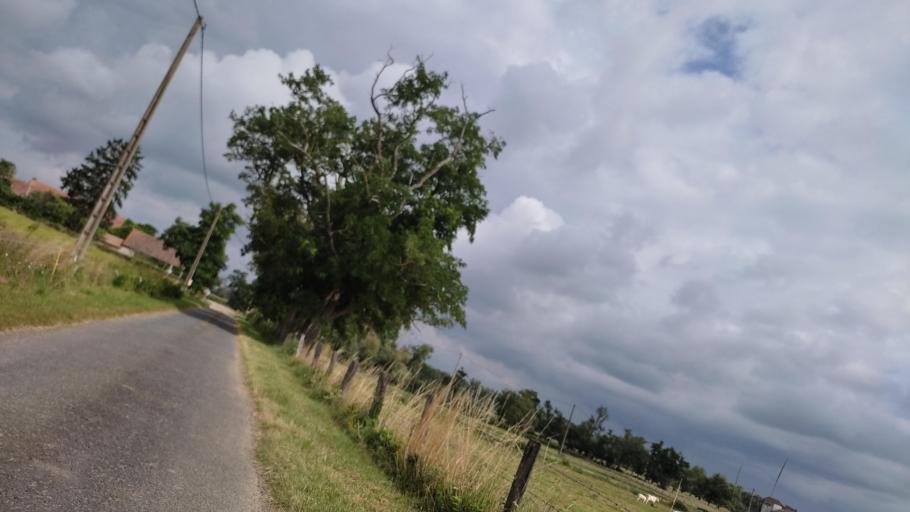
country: FR
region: Auvergne
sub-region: Departement de l'Allier
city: Beaulon
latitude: 46.7275
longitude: 3.6301
